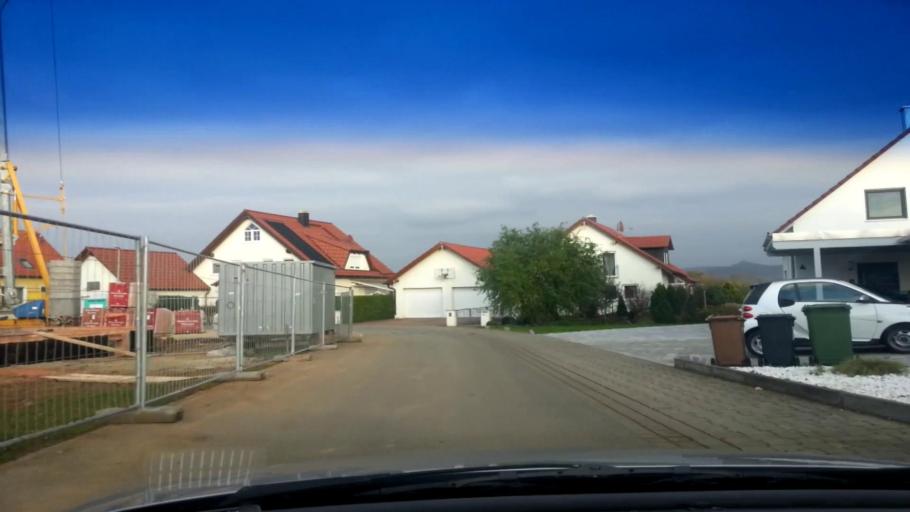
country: DE
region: Bavaria
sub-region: Upper Franconia
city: Memmelsdorf
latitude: 49.9476
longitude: 10.9748
